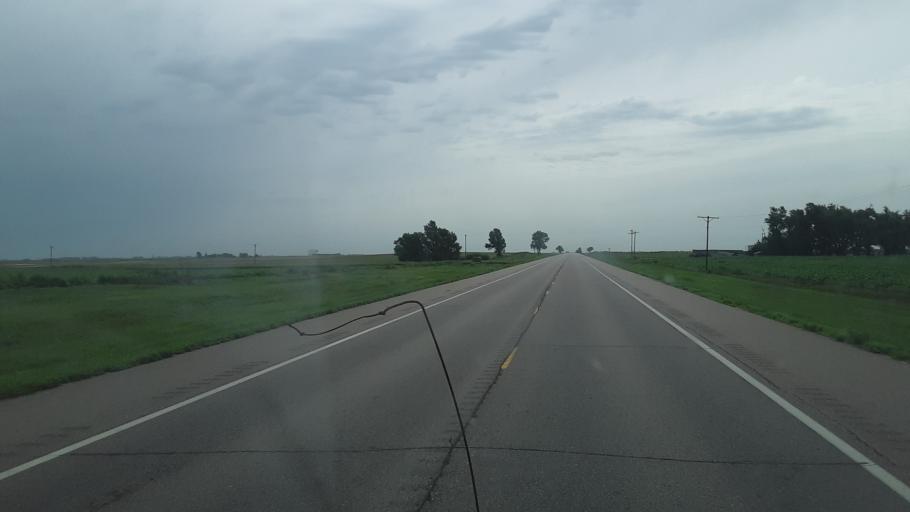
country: US
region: Kansas
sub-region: Stafford County
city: Saint John
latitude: 37.9564
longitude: -98.9344
